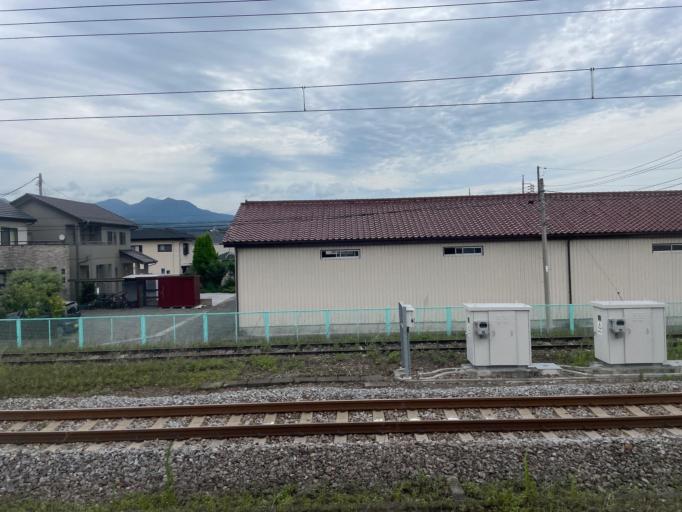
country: JP
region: Gunma
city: Shibukawa
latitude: 36.4617
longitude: 139.0196
